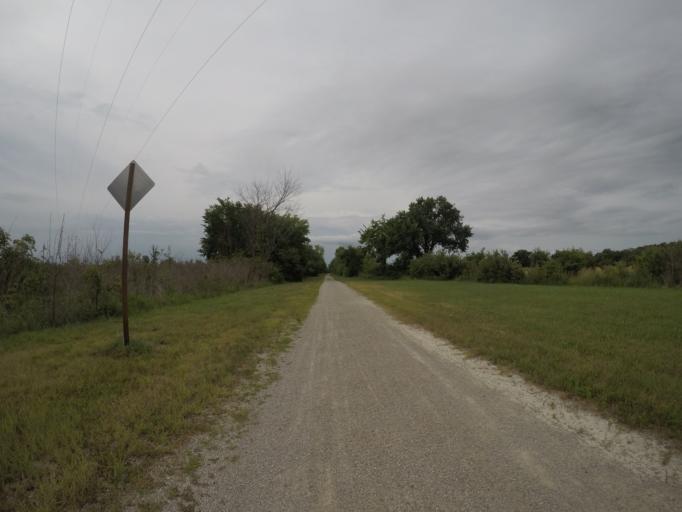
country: US
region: Kansas
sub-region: Franklin County
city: Ottawa
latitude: 38.5644
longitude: -95.2712
